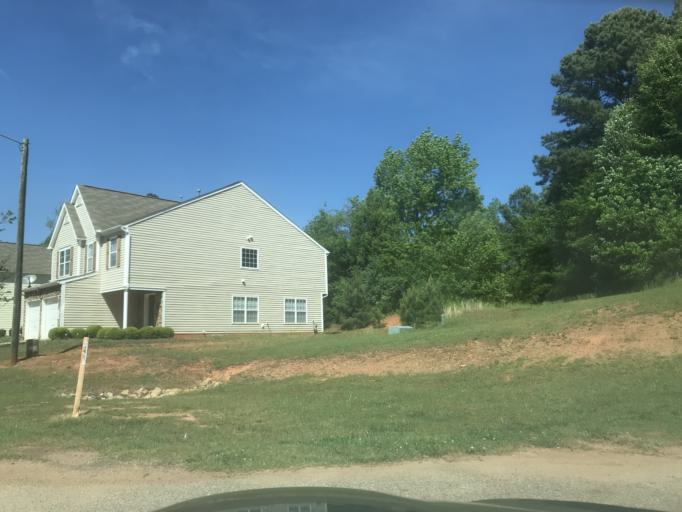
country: US
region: North Carolina
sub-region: Wake County
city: Garner
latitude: 35.7314
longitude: -78.6222
